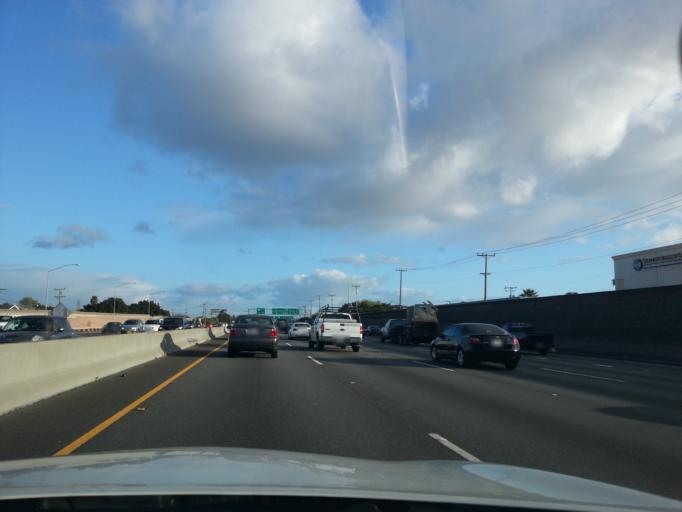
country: US
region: California
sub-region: San Mateo County
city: San Mateo
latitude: 37.5632
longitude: -122.3057
